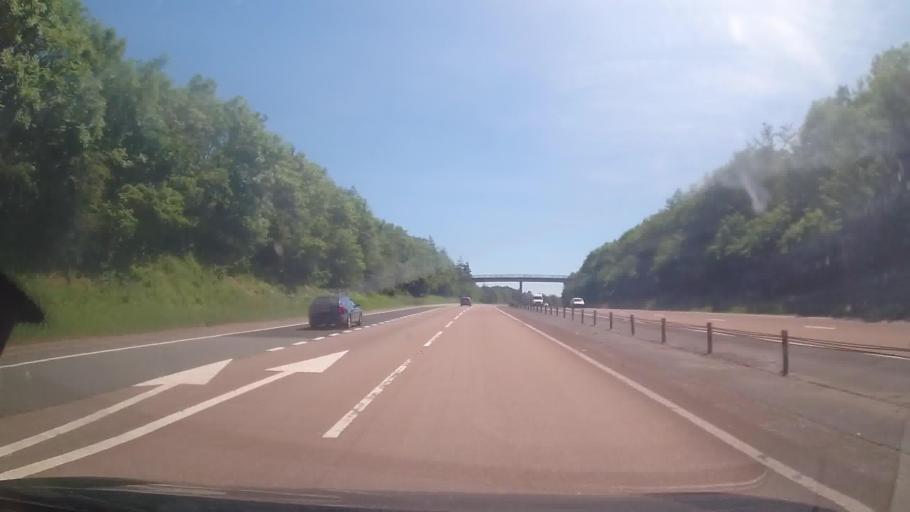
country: GB
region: England
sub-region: Devon
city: Ottery St Mary
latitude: 50.7561
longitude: -3.3284
